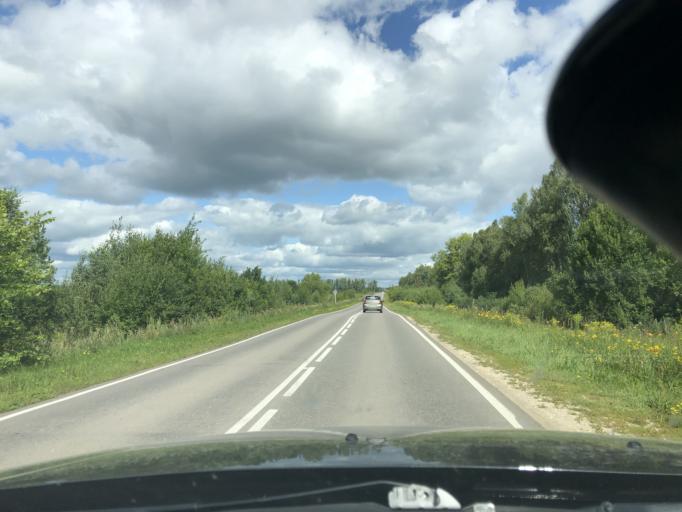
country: RU
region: Tula
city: Yasnogorsk
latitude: 54.4553
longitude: 37.7120
